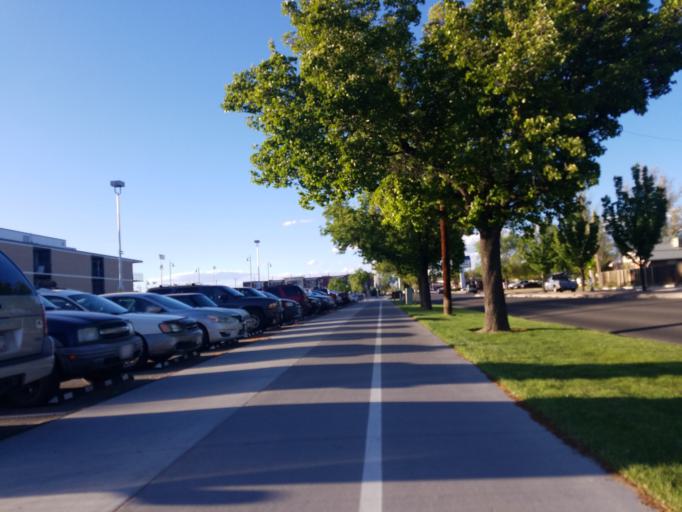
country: US
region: Colorado
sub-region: Mesa County
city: Grand Junction
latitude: 39.0820
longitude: -108.5525
